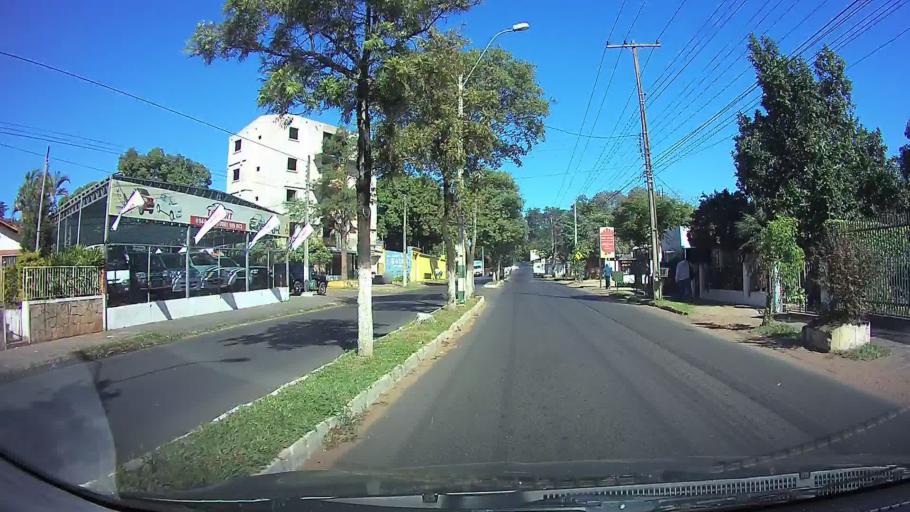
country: PY
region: Central
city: Villa Elisa
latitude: -25.3606
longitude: -57.5750
